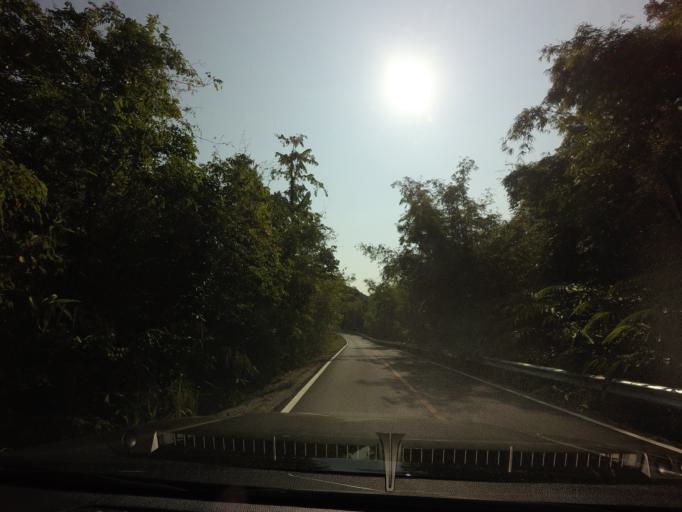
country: TH
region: Kanchanaburi
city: Thong Pha Phum
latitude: 14.6900
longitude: 98.4089
